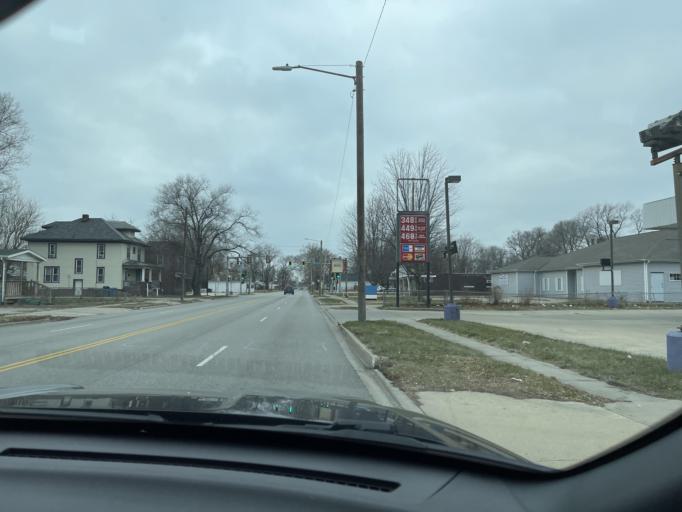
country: US
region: Illinois
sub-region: Sangamon County
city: Springfield
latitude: 39.7947
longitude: -89.6342
